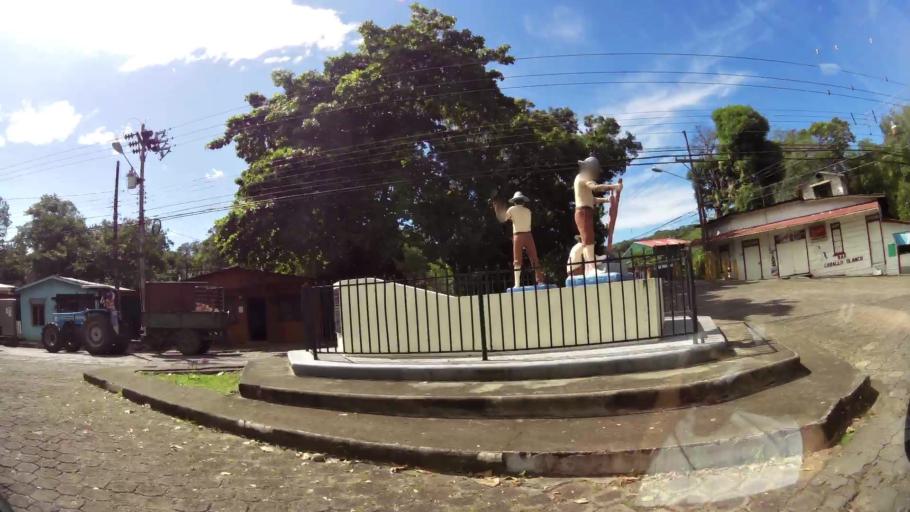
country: CR
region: Guanacaste
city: Juntas
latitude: 10.2820
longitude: -84.9560
